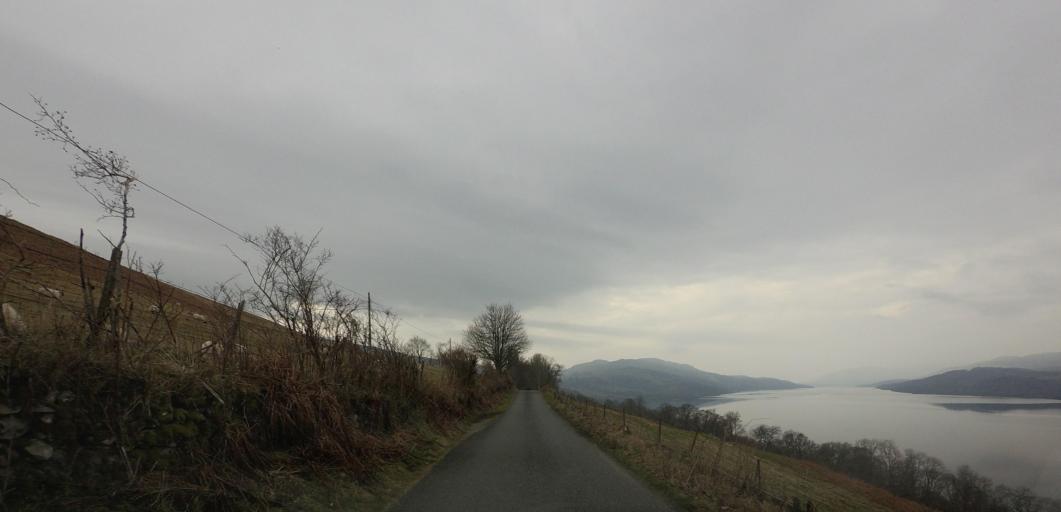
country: GB
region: Scotland
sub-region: Perth and Kinross
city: Comrie
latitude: 56.5143
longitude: -4.1315
